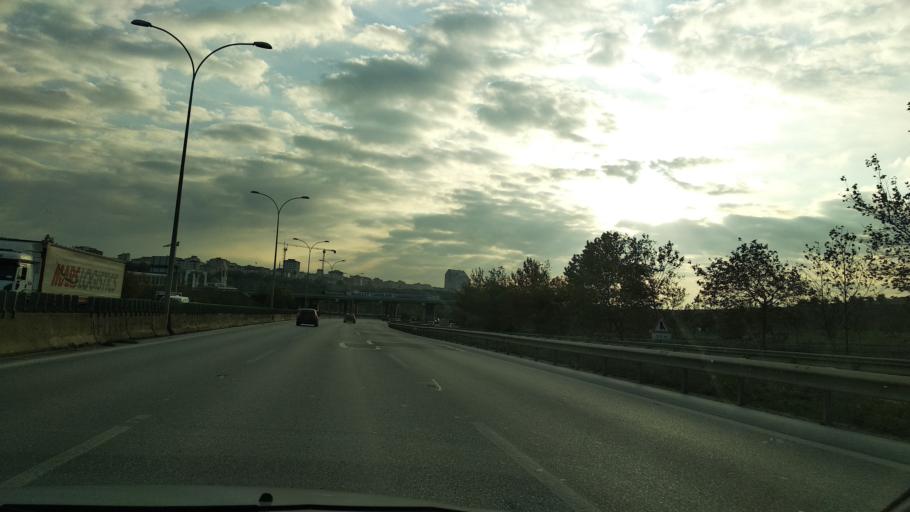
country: TR
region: Istanbul
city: Icmeler
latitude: 40.8806
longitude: 29.3160
